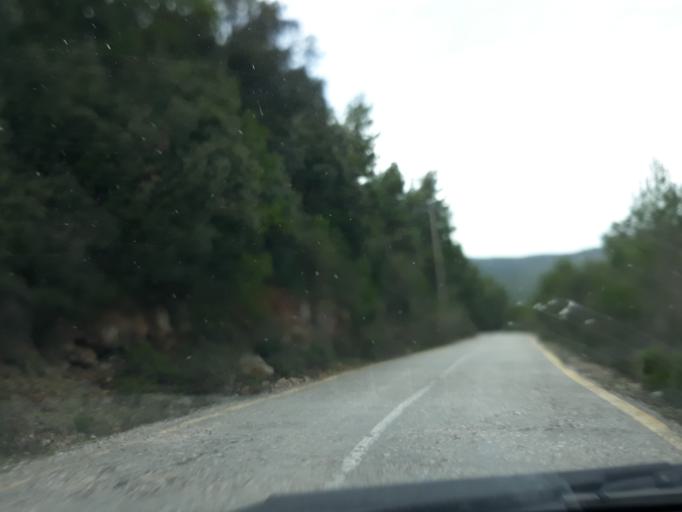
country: GR
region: Attica
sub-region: Nomarchia Anatolikis Attikis
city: Afidnes
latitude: 38.1866
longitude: 23.7908
